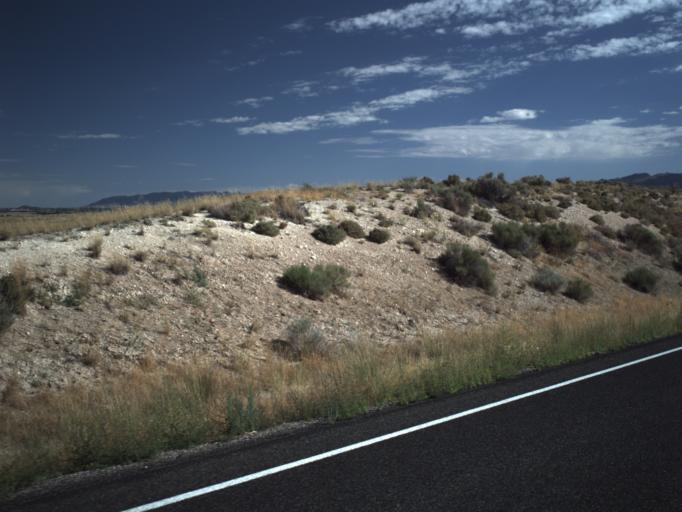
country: US
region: Utah
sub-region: Juab County
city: Mona
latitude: 39.7063
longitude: -112.2110
